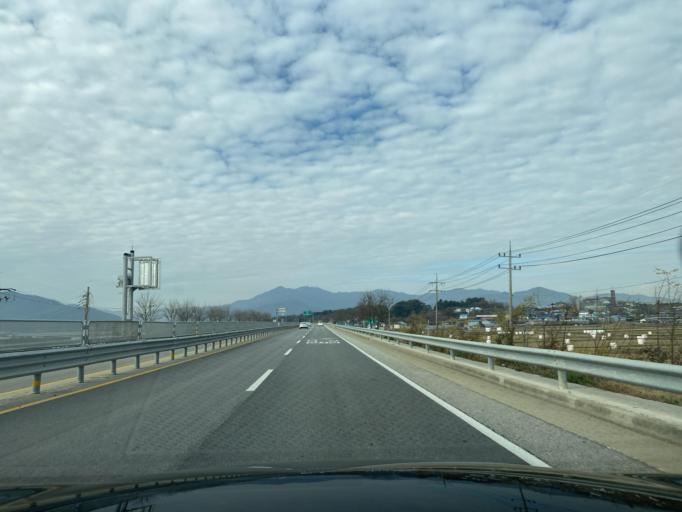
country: KR
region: Chungcheongnam-do
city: Hongsung
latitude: 36.6905
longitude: 126.7027
